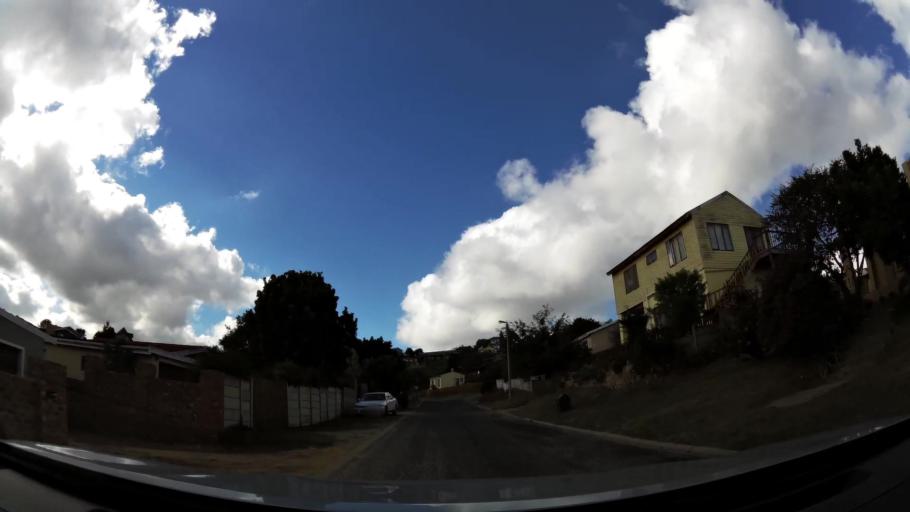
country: ZA
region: Western Cape
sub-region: Eden District Municipality
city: Knysna
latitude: -34.0461
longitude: 23.0848
